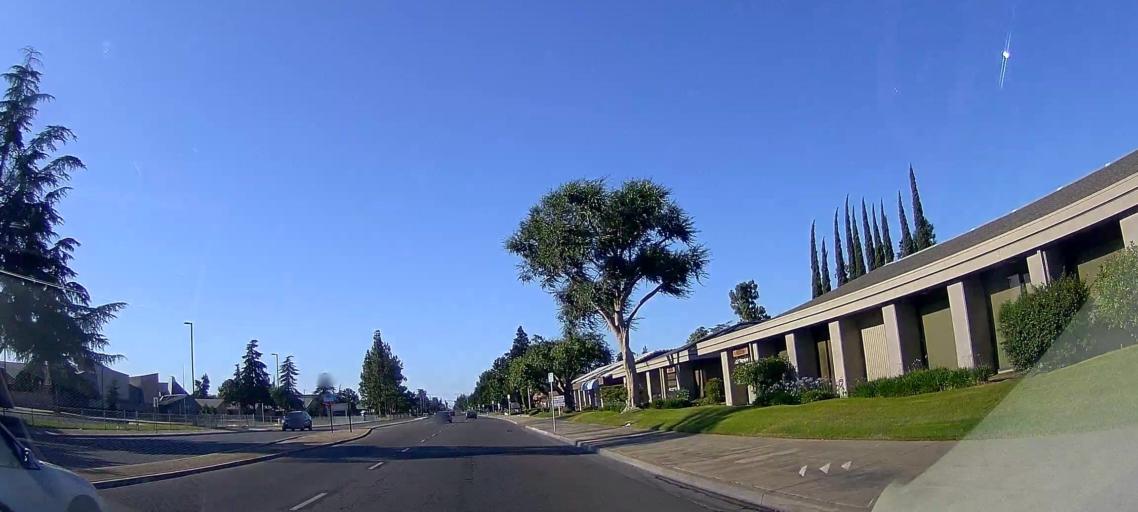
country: US
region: California
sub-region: Fresno County
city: Fresno
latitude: 36.8159
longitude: -119.8083
